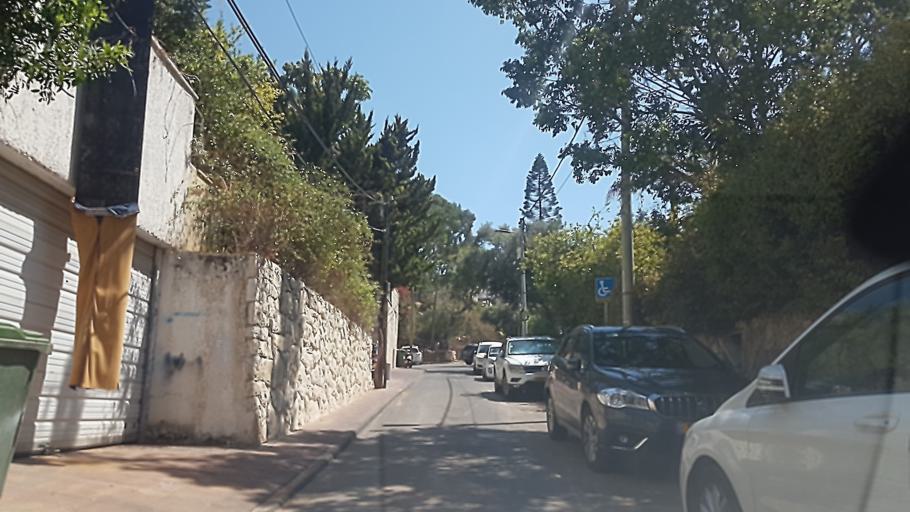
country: IL
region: Tel Aviv
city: Bene Beraq
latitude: 32.0821
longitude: 34.8238
